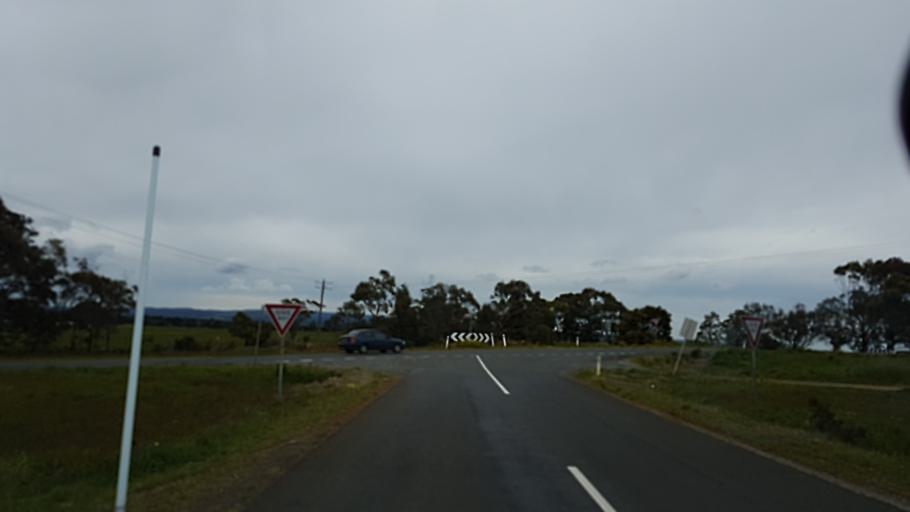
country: AU
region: Victoria
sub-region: Moorabool
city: Bacchus Marsh
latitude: -37.6245
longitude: 144.2099
